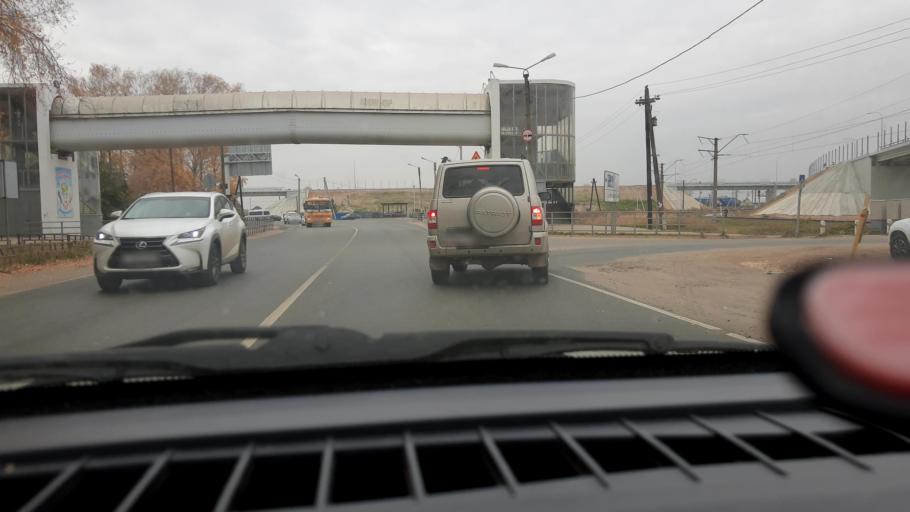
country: RU
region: Nizjnij Novgorod
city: Neklyudovo
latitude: 56.4008
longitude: 43.9872
